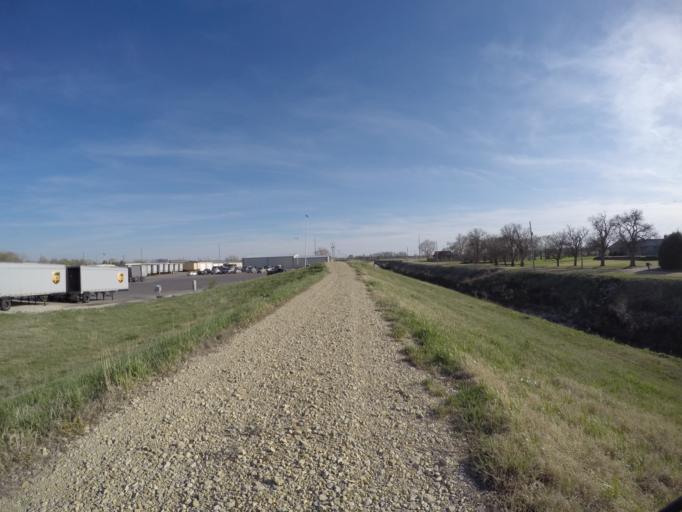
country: US
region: Kansas
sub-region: Saline County
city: Salina
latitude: 38.8510
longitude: -97.6303
